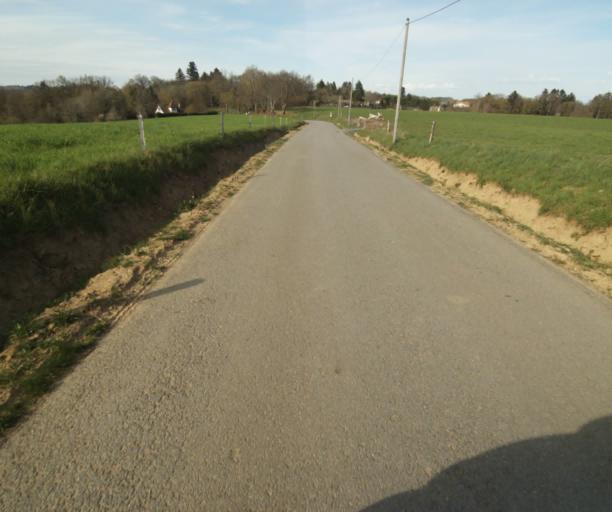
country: FR
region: Limousin
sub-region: Departement de la Correze
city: Naves
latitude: 45.3015
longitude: 1.7385
